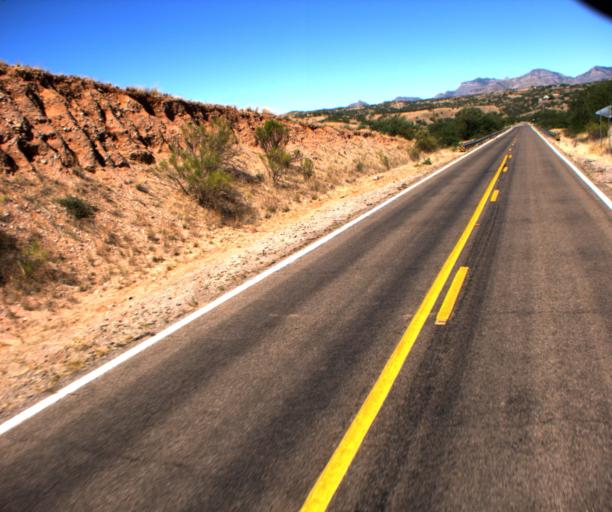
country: US
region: Arizona
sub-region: Santa Cruz County
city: Rio Rico
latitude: 31.4297
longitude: -110.9937
